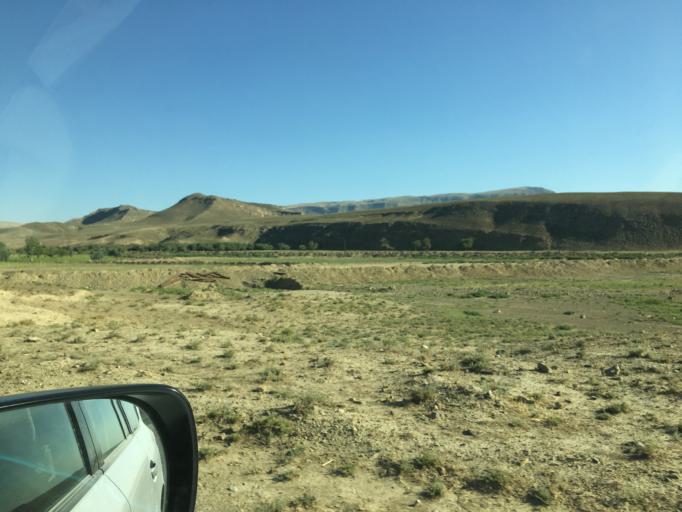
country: TM
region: Balkan
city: Magtymguly
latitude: 38.6300
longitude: 56.6267
